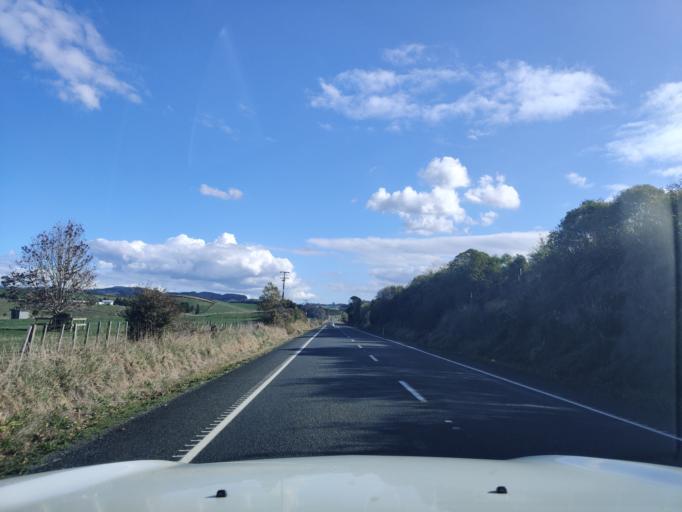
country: NZ
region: Waikato
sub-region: Hauraki District
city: Ngatea
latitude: -37.2840
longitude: 175.3975
